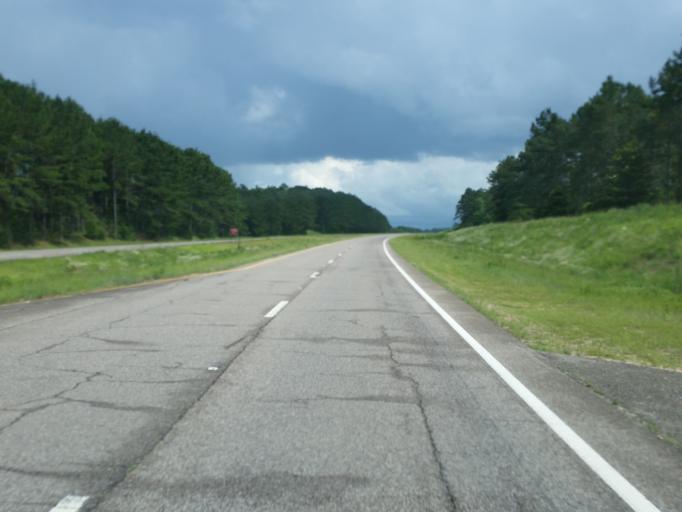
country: US
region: Mississippi
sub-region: George County
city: Lucedale
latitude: 30.9421
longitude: -88.5309
